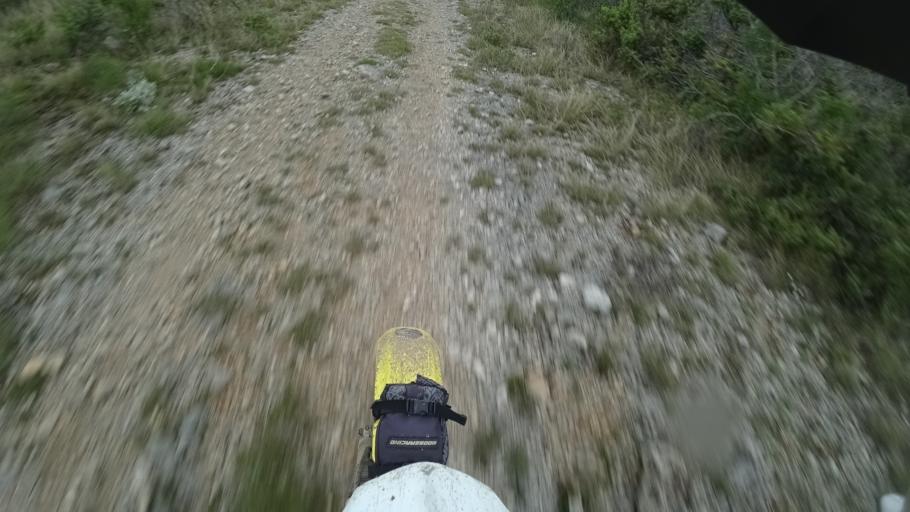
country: HR
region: Sibensko-Kniniska
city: Knin
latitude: 44.0331
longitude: 16.2422
